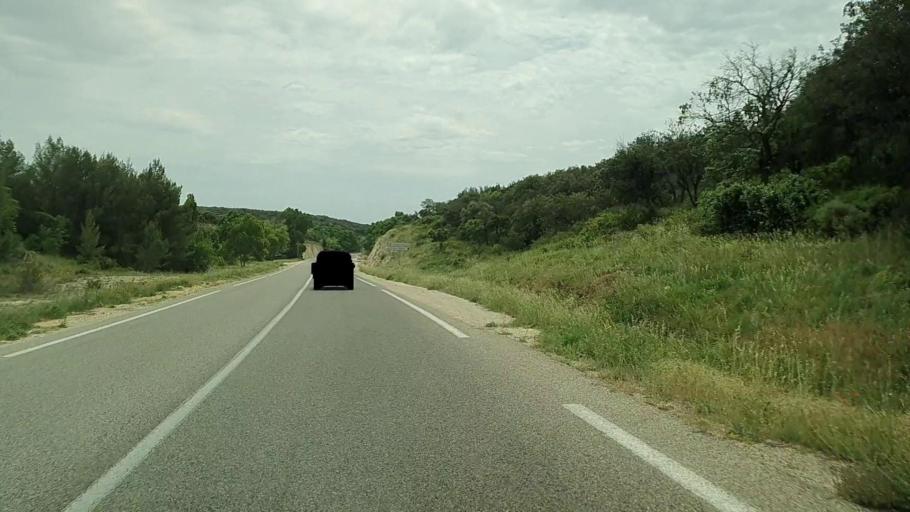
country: FR
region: Languedoc-Roussillon
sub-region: Departement du Gard
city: Connaux
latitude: 44.0310
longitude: 4.5811
